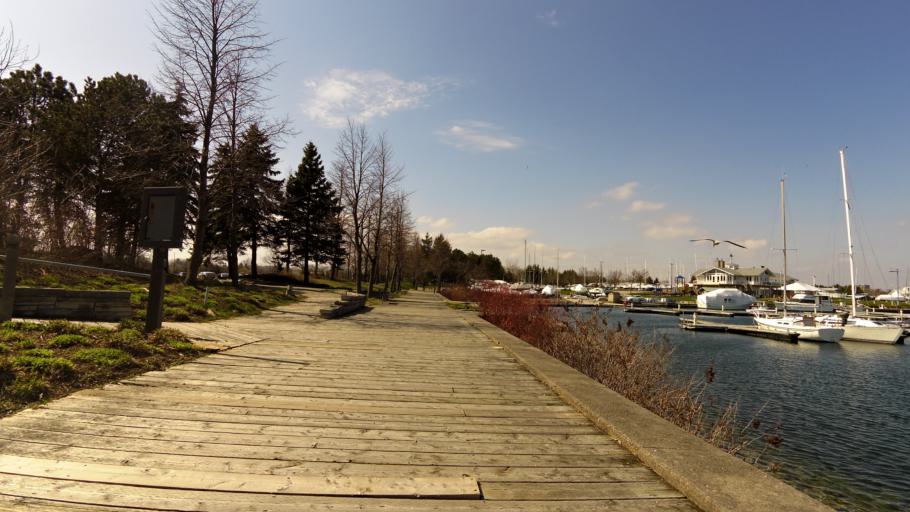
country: CA
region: Ontario
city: Etobicoke
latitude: 43.5633
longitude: -79.5574
